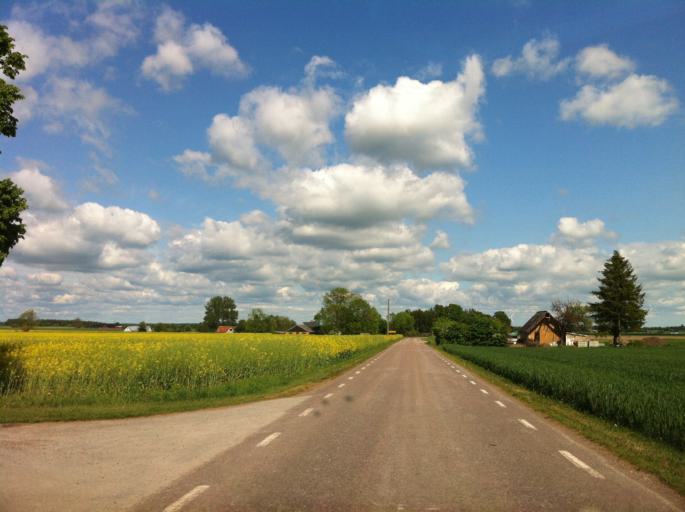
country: SE
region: Skane
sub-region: Landskrona
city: Asmundtorp
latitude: 55.9605
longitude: 12.9062
